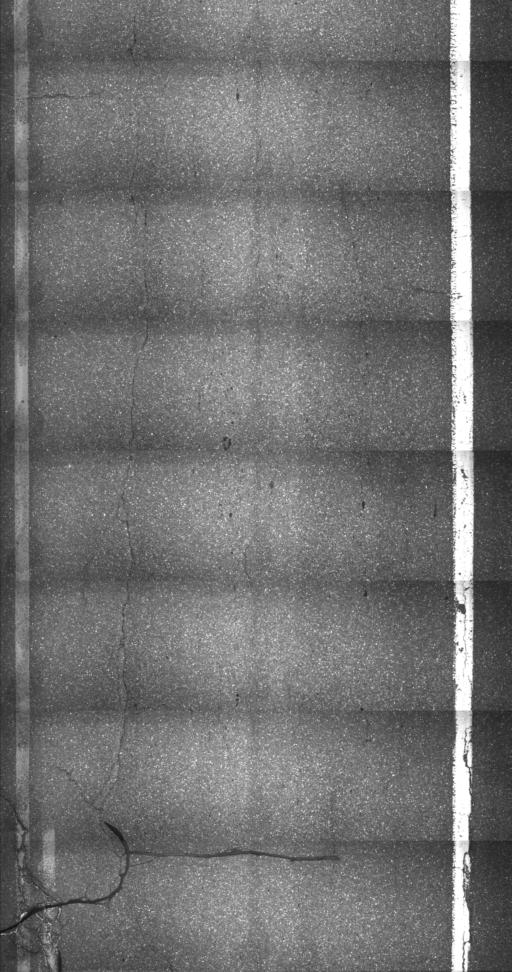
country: US
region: Vermont
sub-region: Caledonia County
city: Hardwick
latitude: 44.4483
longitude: -72.2331
